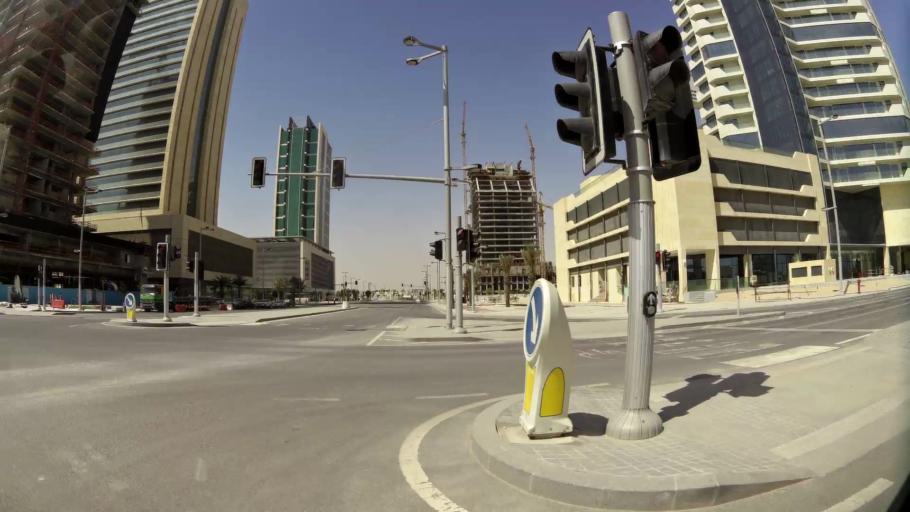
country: QA
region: Baladiyat ad Dawhah
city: Doha
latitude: 25.3904
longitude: 51.5232
